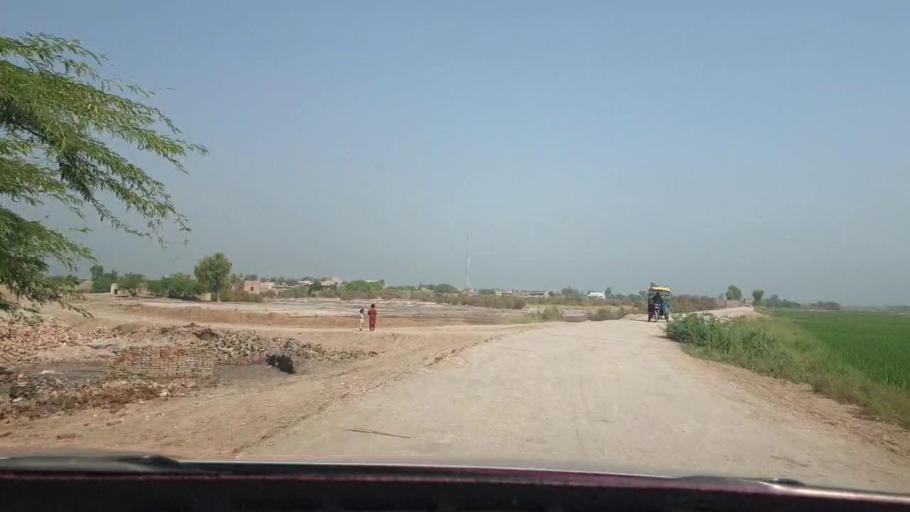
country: PK
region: Sindh
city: Nasirabad
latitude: 27.4201
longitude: 67.9288
